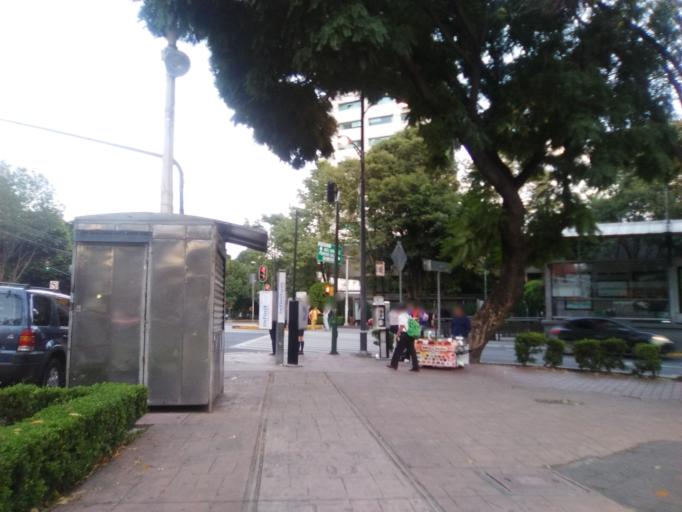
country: MX
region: Mexico City
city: Colonia del Valle
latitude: 19.3799
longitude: -99.1773
